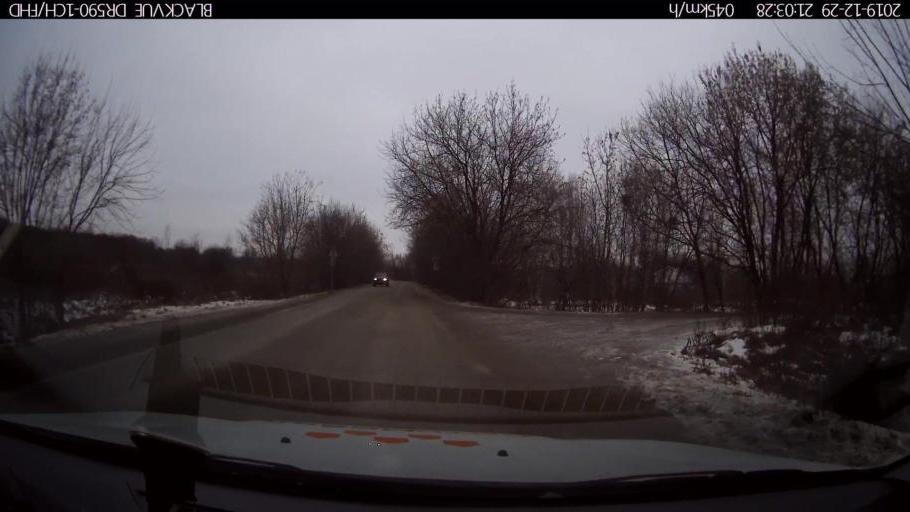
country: RU
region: Nizjnij Novgorod
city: Afonino
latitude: 56.1954
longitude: 44.0056
